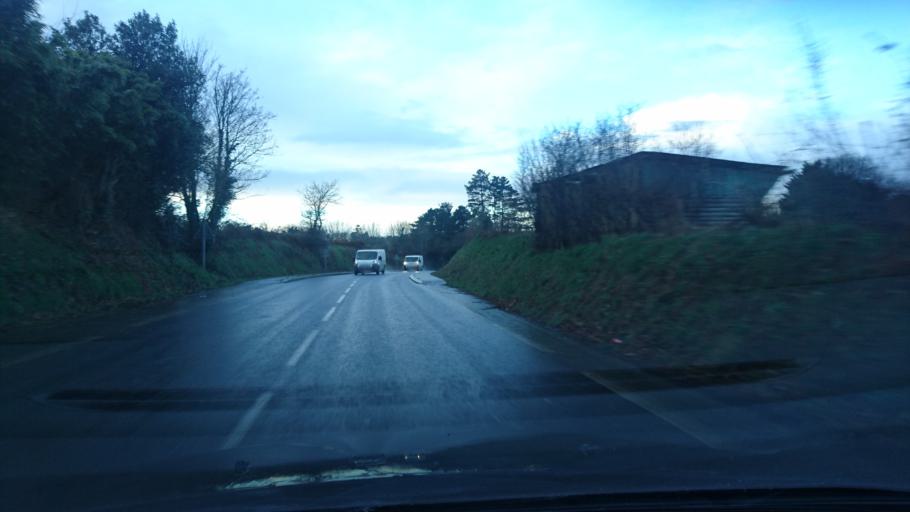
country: FR
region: Brittany
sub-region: Departement du Finistere
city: Guilers
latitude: 48.4002
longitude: -4.5403
